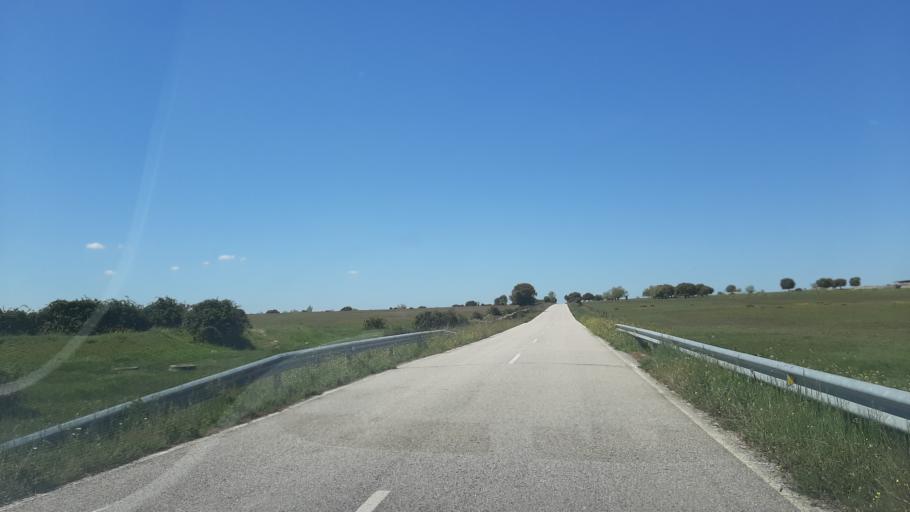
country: ES
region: Castille and Leon
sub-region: Provincia de Salamanca
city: Villarmuerto
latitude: 41.0523
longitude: -6.3719
